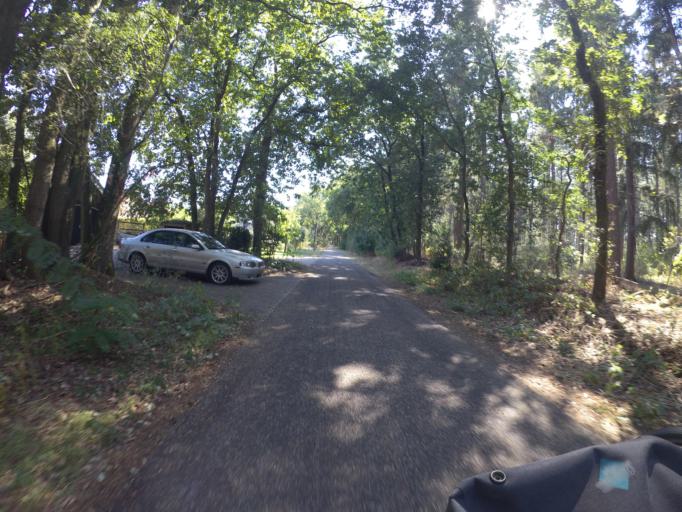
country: NL
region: Overijssel
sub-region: Gemeente Twenterand
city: Den Ham
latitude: 52.4055
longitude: 6.4291
